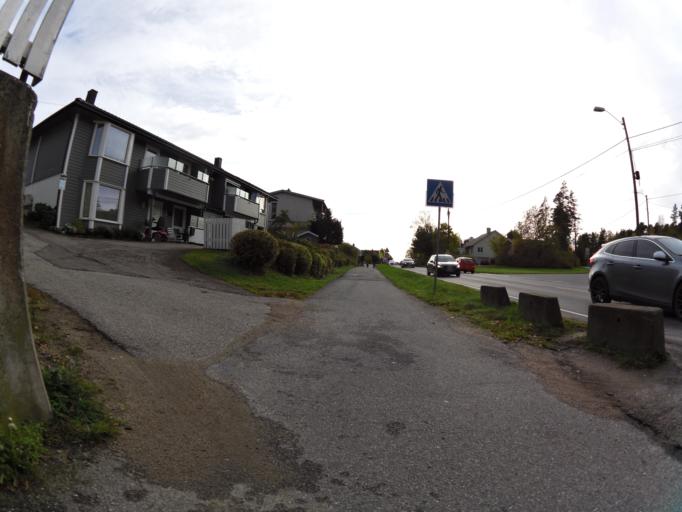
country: NO
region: Ostfold
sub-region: Fredrikstad
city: Fredrikstad
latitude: 59.2258
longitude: 10.9104
